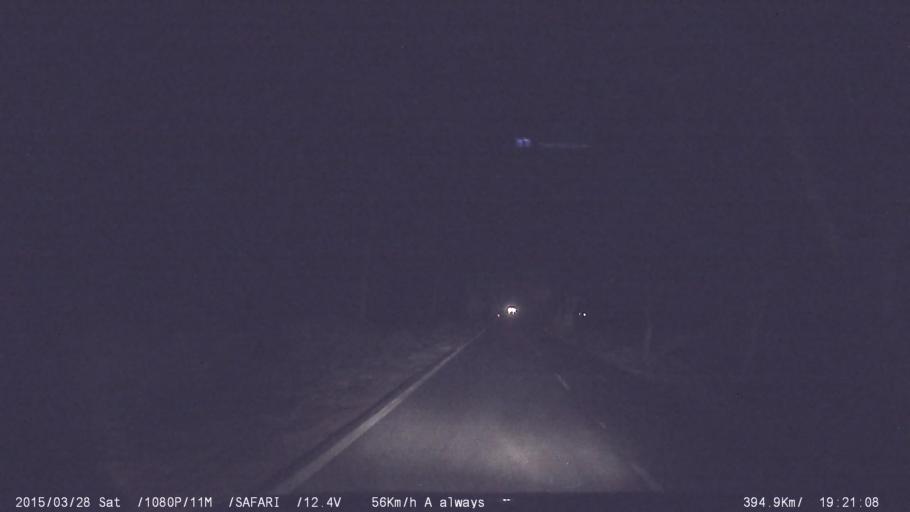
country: IN
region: Karnataka
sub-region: Mandya
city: Shrirangapattana
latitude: 12.4183
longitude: 76.6635
